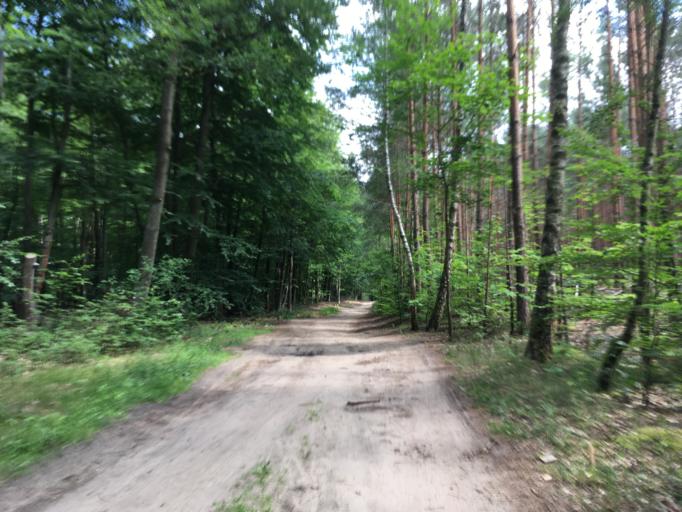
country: DE
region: Brandenburg
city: Wandlitz
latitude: 52.7319
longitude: 13.4532
